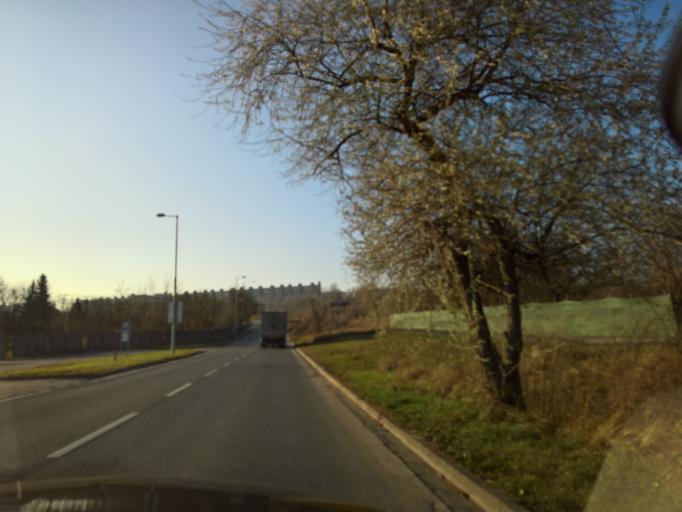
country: SK
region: Nitriansky
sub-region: Okres Nitra
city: Nitra
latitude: 48.3133
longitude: 18.0509
